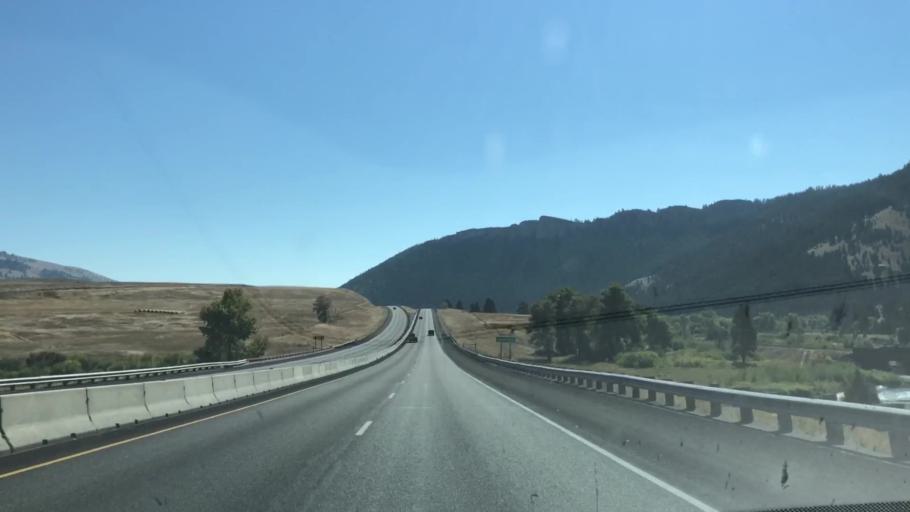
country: US
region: Montana
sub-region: Granite County
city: Philipsburg
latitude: 46.7019
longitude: -113.2436
